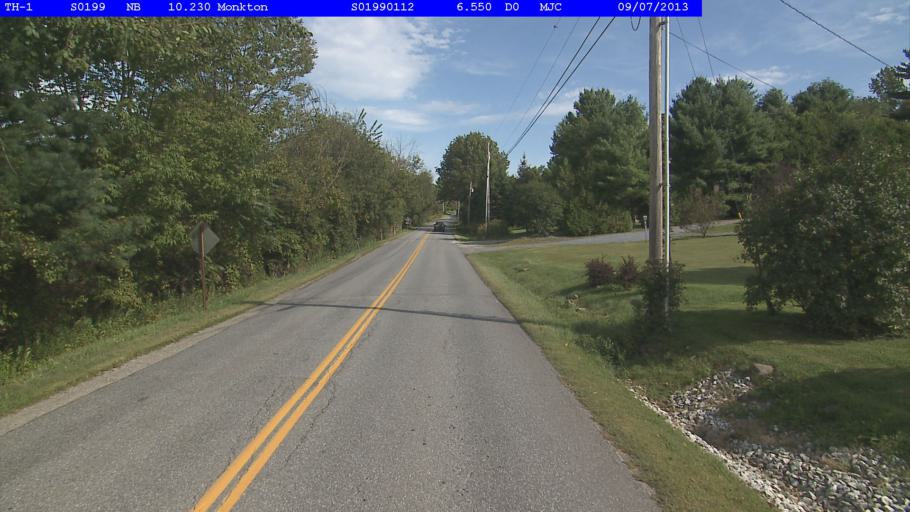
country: US
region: Vermont
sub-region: Chittenden County
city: Hinesburg
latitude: 44.2709
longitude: -73.1114
